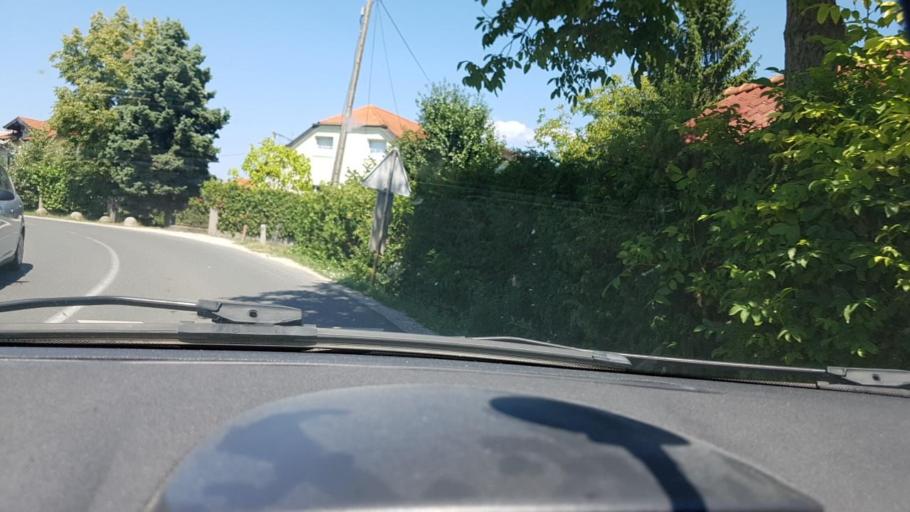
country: HR
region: Grad Zagreb
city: Brezovica
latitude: 45.7448
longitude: 15.8891
